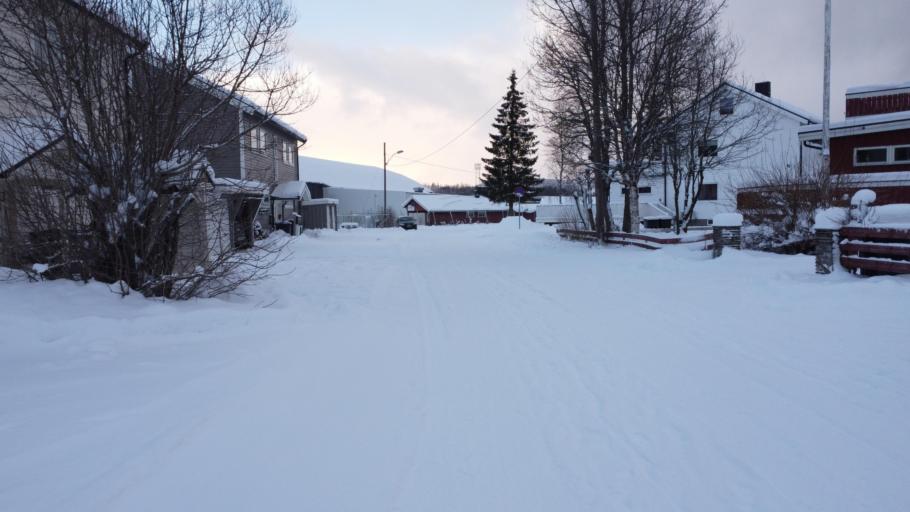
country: NO
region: Nordland
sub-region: Rana
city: Mo i Rana
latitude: 66.3202
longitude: 14.1627
